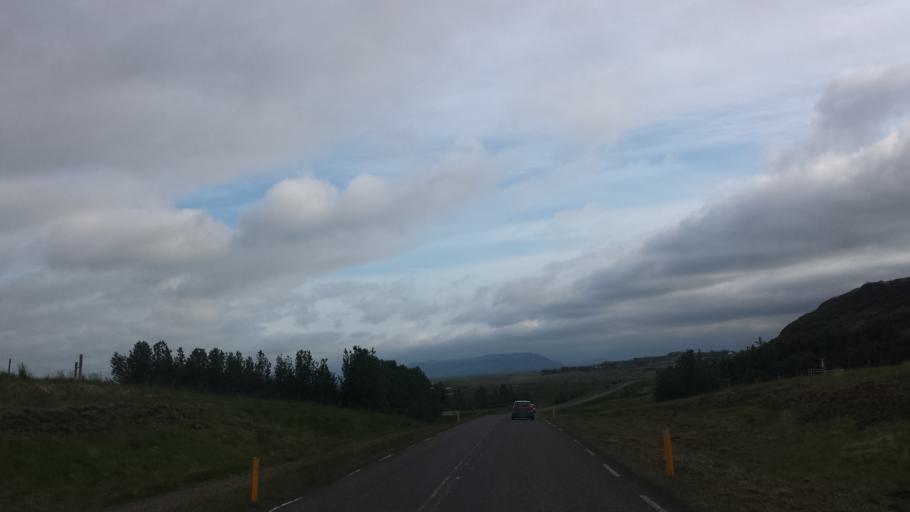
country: IS
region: South
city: Selfoss
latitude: 64.1984
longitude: -20.3958
